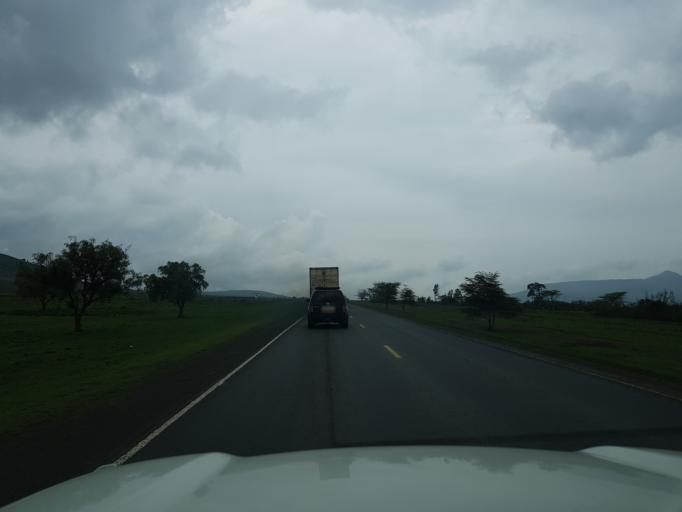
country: KE
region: Nakuru
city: Naivasha
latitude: -0.8301
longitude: 36.4718
